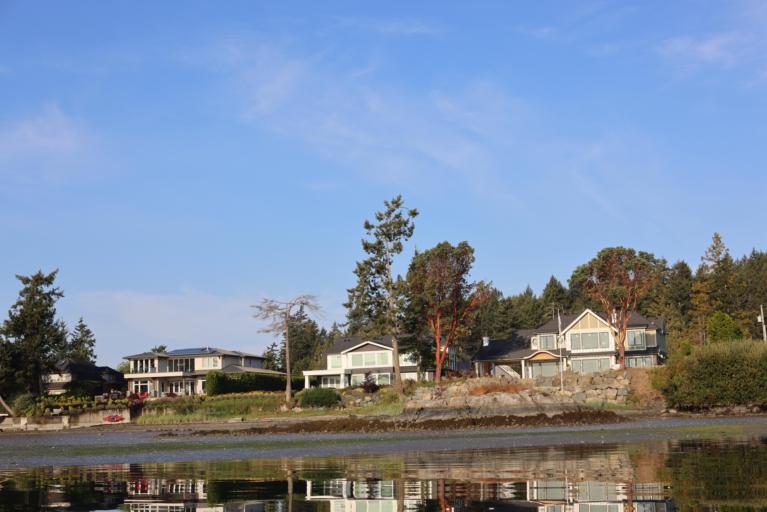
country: CA
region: British Columbia
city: North Saanich
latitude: 48.6741
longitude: -123.4194
